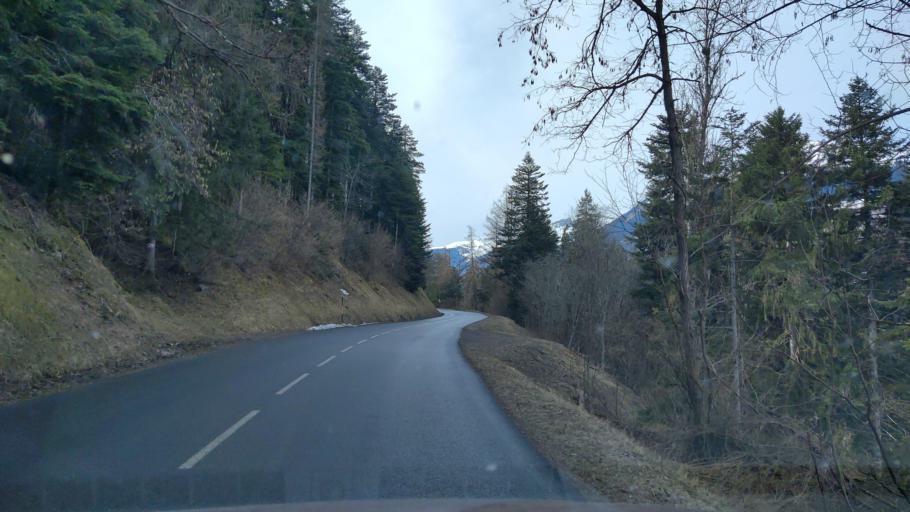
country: FR
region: Rhone-Alpes
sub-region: Departement de la Savoie
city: Macot-la-Plagne
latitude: 45.5615
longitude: 6.6950
